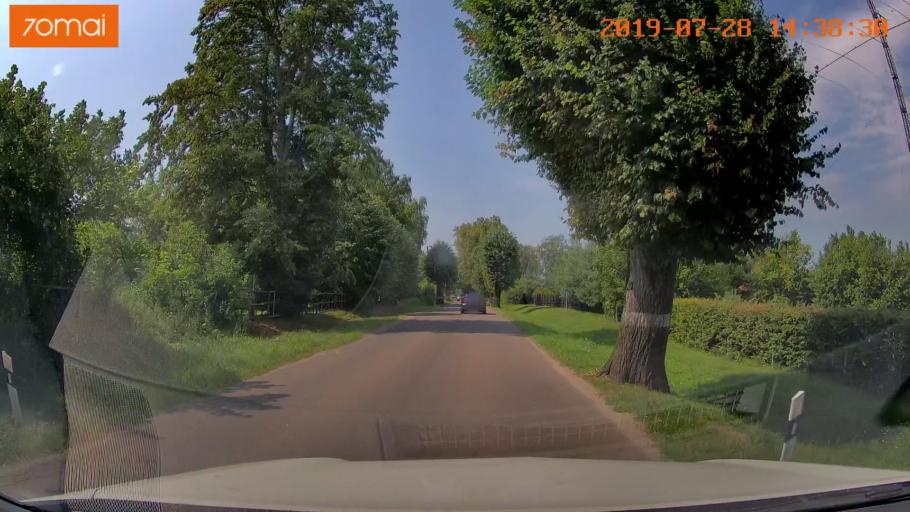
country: RU
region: Kaliningrad
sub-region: Gorod Kaliningrad
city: Yantarnyy
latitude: 54.8450
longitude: 19.9832
